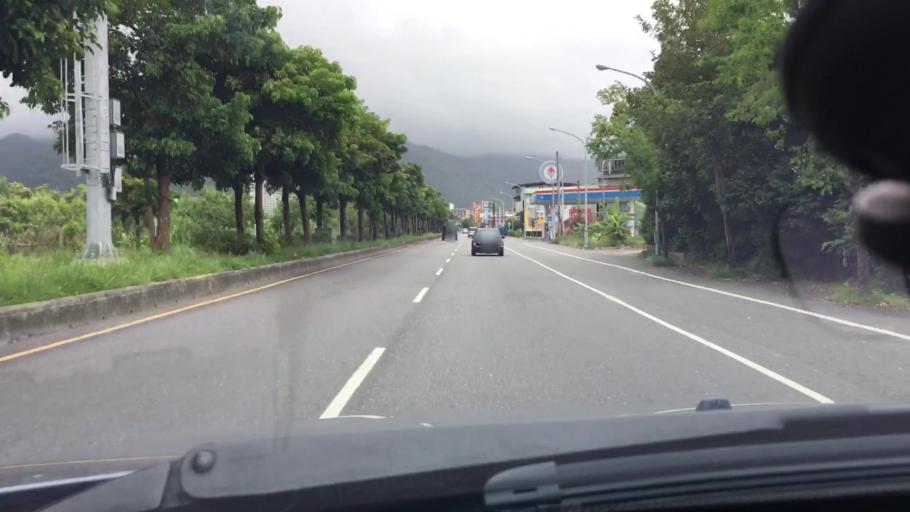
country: TW
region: Taiwan
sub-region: Yilan
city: Yilan
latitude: 24.8105
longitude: 121.7672
